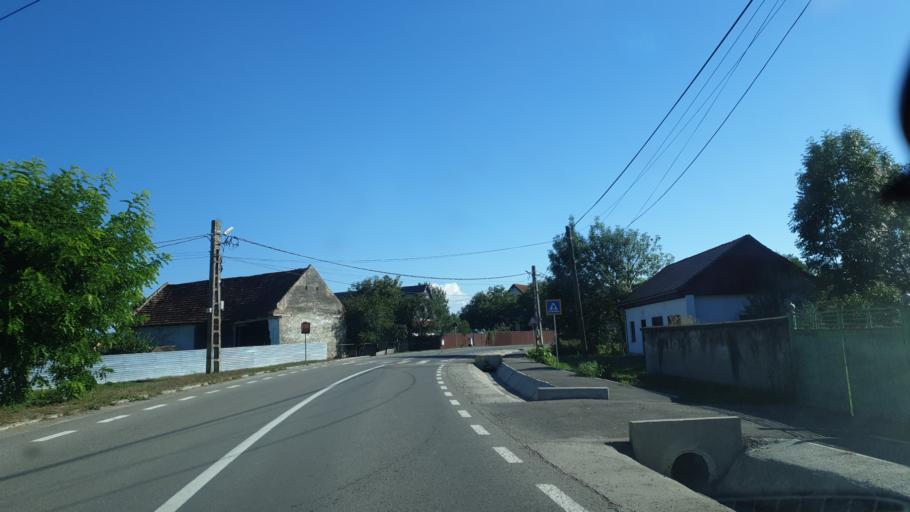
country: RO
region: Covasna
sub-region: Comuna Ilieni
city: Ilieni
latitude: 45.7969
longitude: 25.7714
